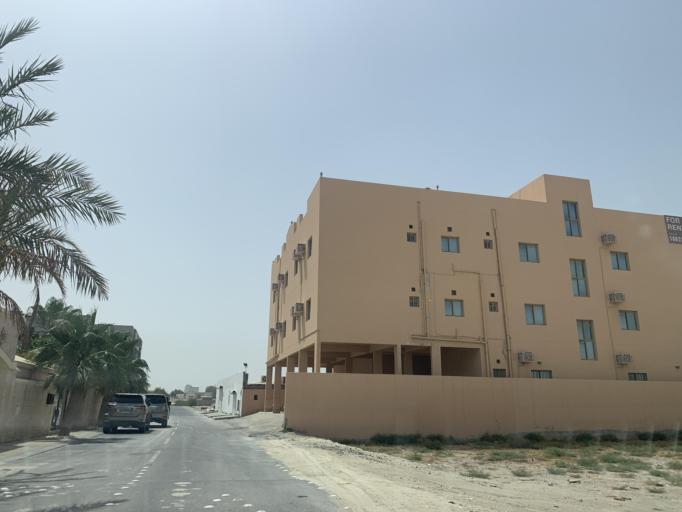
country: BH
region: Northern
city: Madinat `Isa
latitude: 26.1582
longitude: 50.5287
